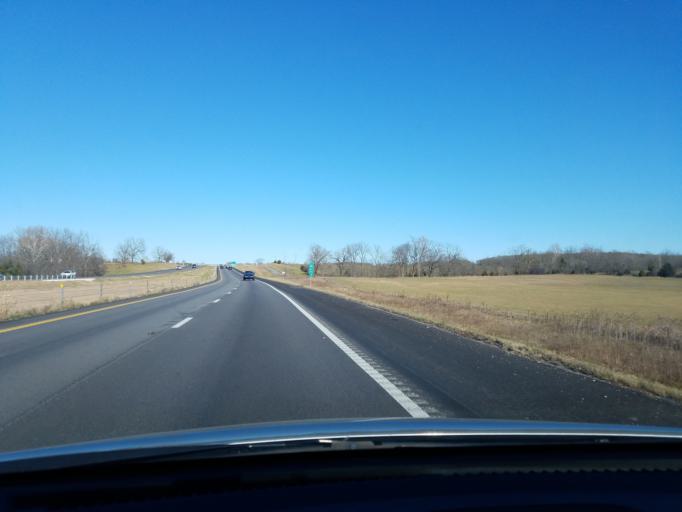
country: US
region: Missouri
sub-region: Webster County
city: Marshfield
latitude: 37.4110
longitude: -92.8892
